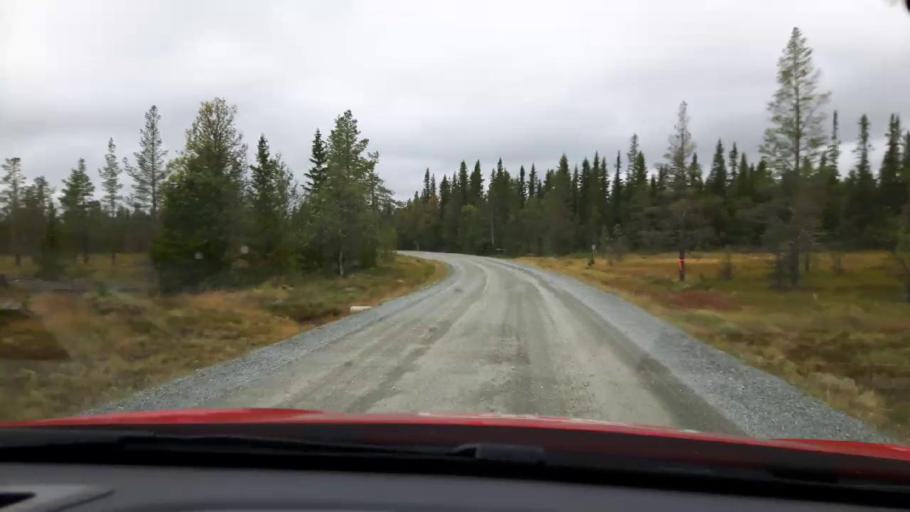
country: SE
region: Jaemtland
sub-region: Bergs Kommun
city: Hoverberg
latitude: 62.9124
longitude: 14.0933
